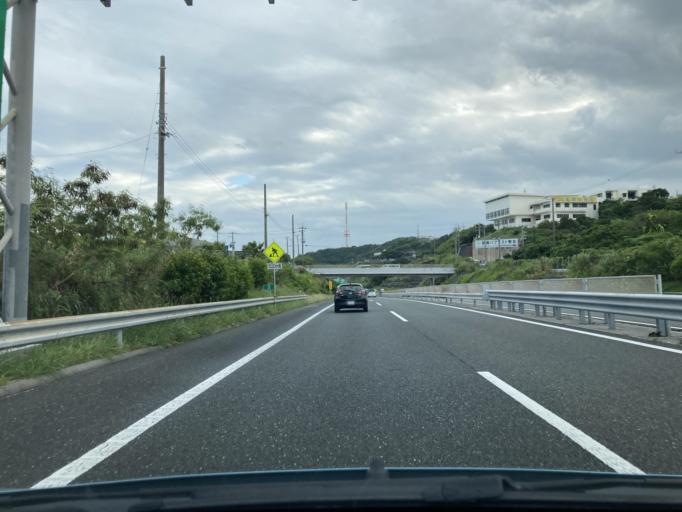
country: JP
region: Okinawa
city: Ginowan
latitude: 26.2285
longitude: 127.7387
